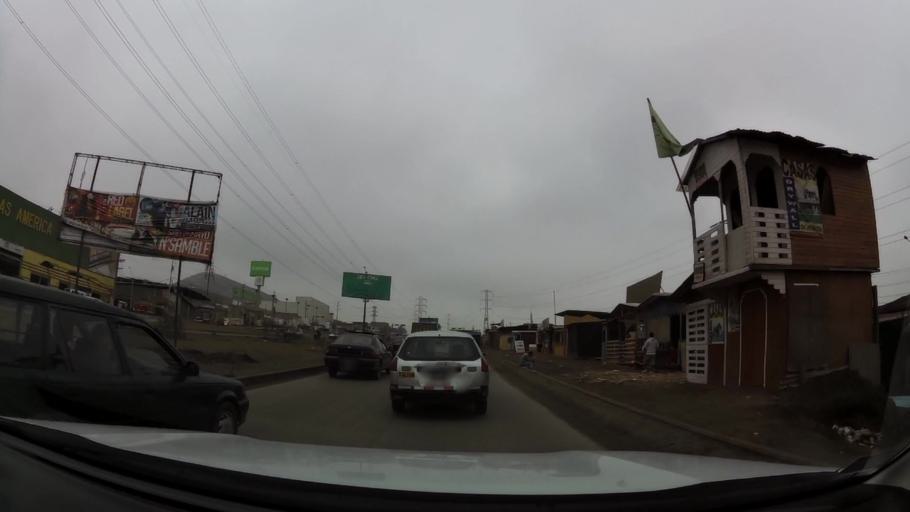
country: PE
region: Lima
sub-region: Lima
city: Surco
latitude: -12.2035
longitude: -76.9299
